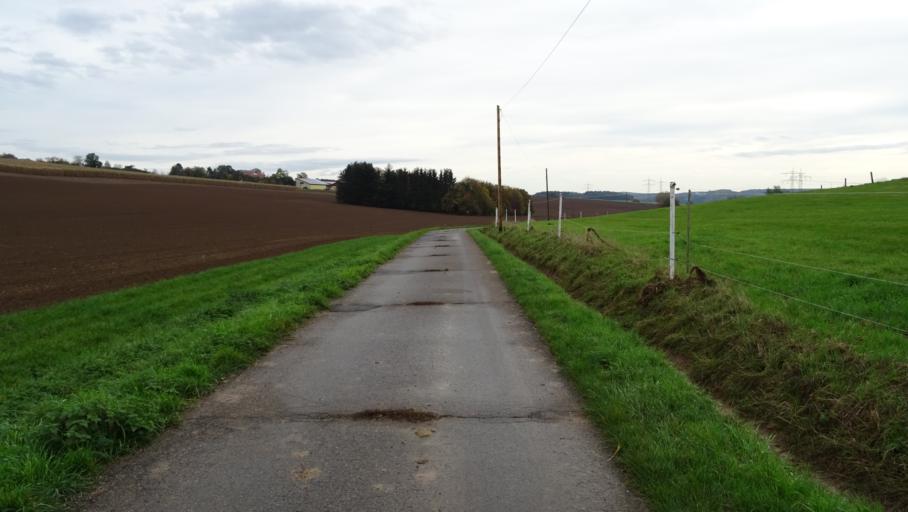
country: DE
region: Baden-Wuerttemberg
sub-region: Karlsruhe Region
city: Billigheim
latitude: 49.3460
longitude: 9.2078
